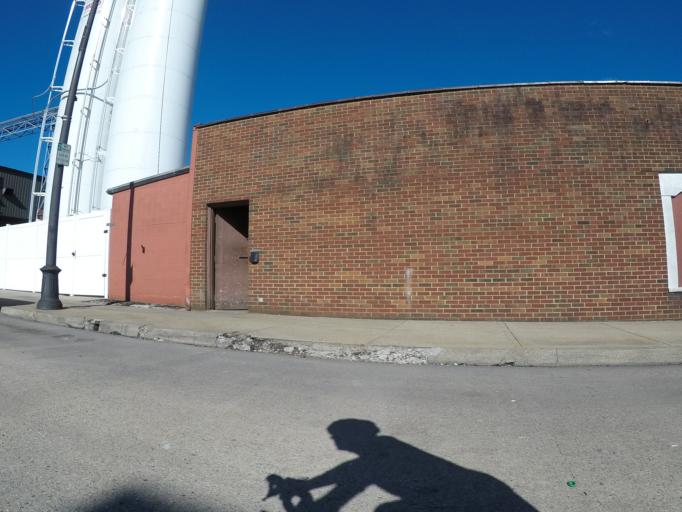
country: US
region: West Virginia
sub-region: Cabell County
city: Huntington
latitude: 38.4121
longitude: -82.4798
